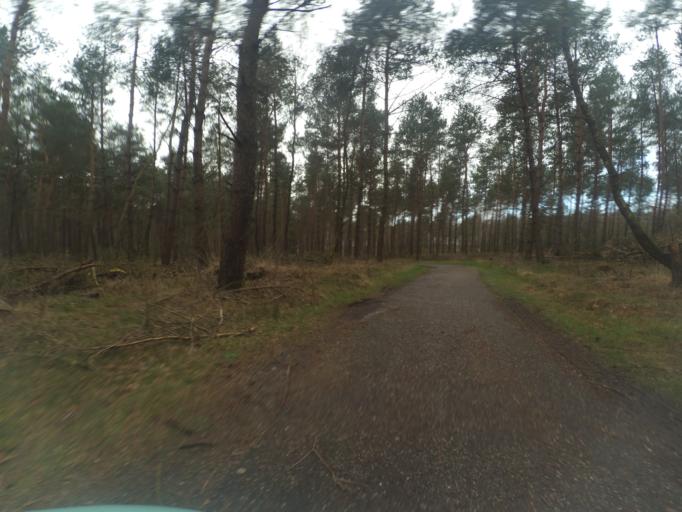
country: NL
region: Gelderland
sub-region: Gemeente Arnhem
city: Gulden Bodem
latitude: 52.0255
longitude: 5.9105
